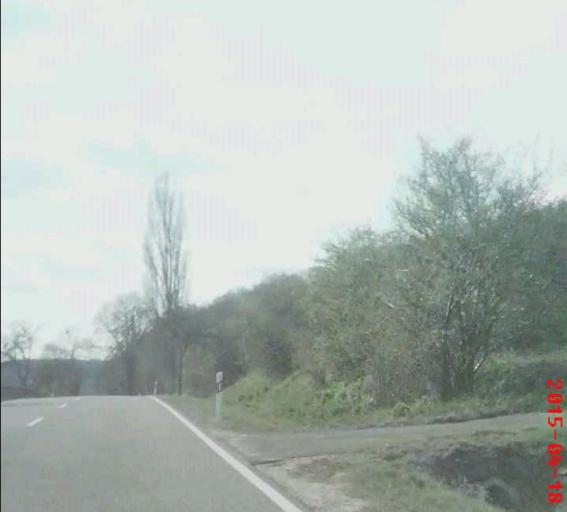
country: DE
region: Thuringia
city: Heuthen
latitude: 51.3458
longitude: 10.2198
